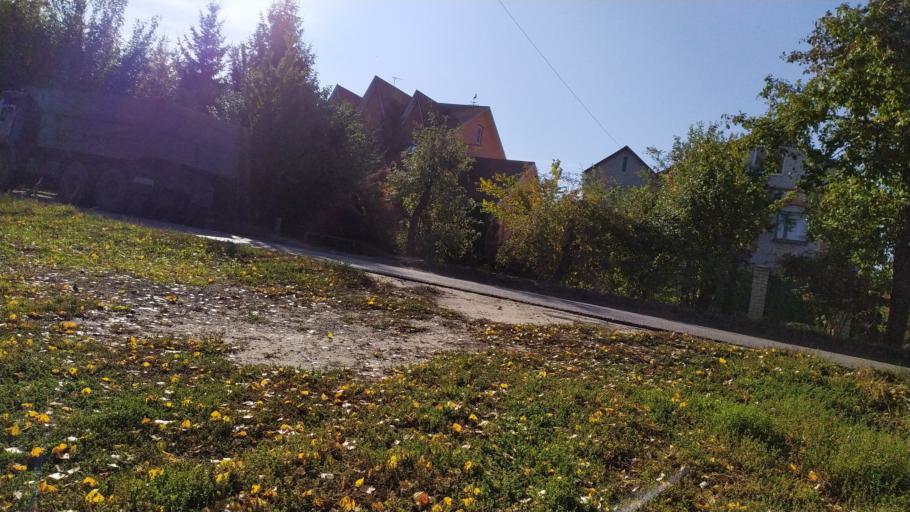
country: RU
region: Kursk
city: Kursk
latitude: 51.6438
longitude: 36.1396
